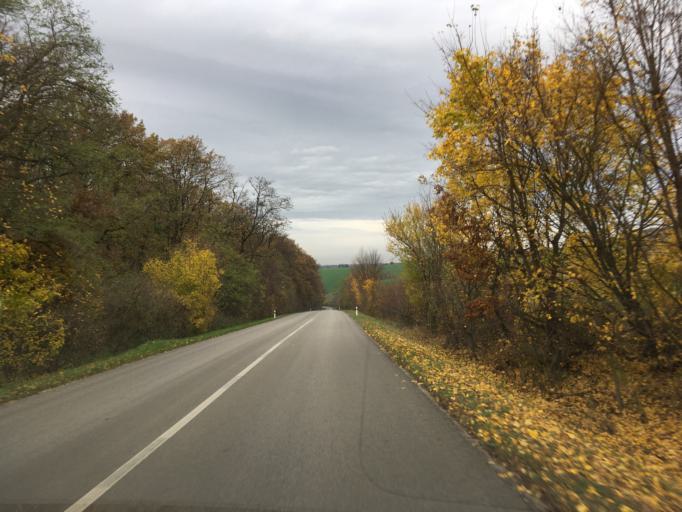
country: SK
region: Nitriansky
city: Svodin
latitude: 48.0309
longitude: 18.3921
